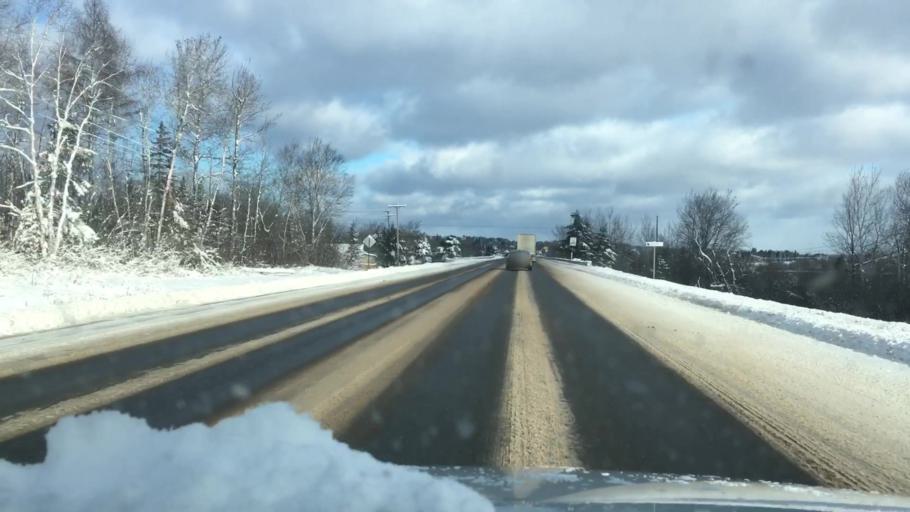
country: US
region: Maine
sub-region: Aroostook County
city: Caribou
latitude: 46.8461
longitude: -68.0040
